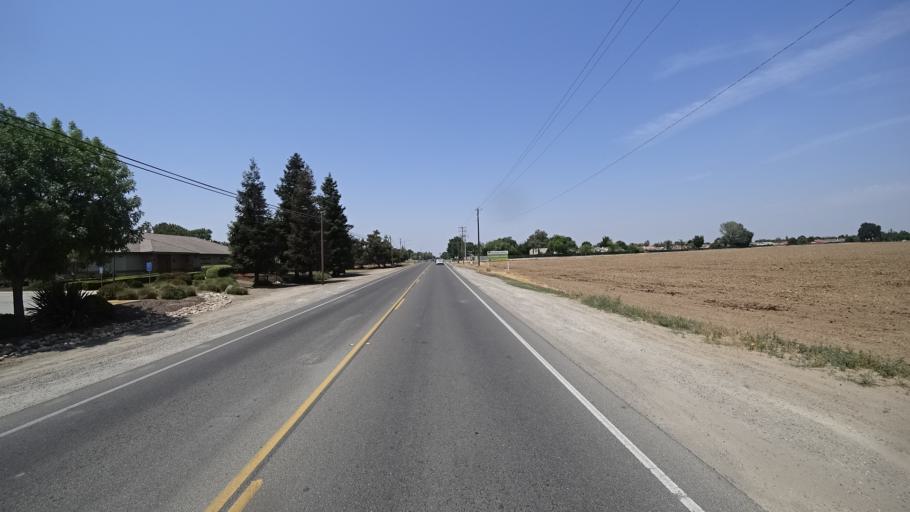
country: US
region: California
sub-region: Kings County
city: Lemoore
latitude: 36.3135
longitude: -119.7630
